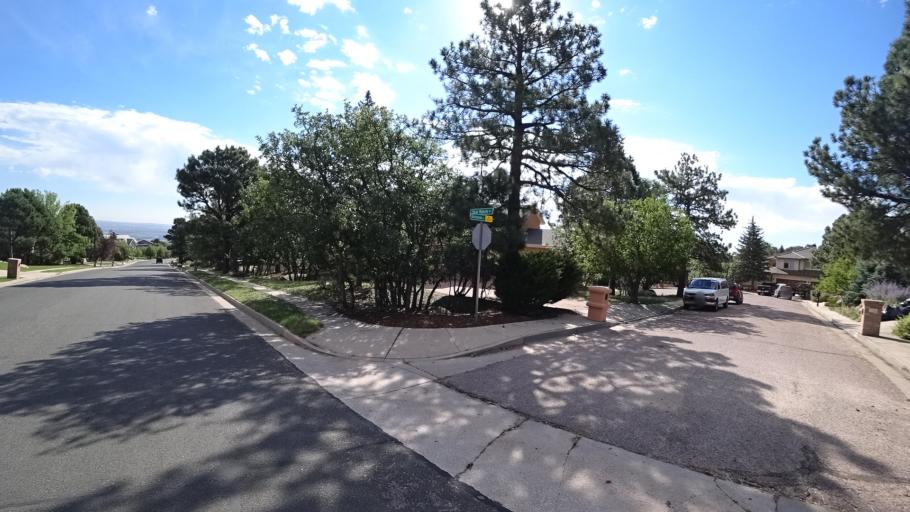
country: US
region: Colorado
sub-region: El Paso County
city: Fort Carson
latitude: 38.7658
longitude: -104.8328
